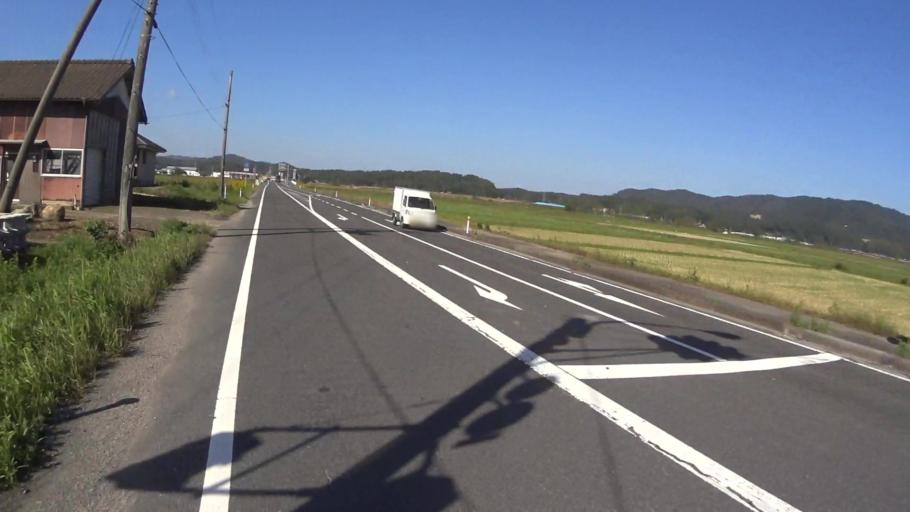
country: JP
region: Kyoto
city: Miyazu
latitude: 35.6695
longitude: 135.0918
